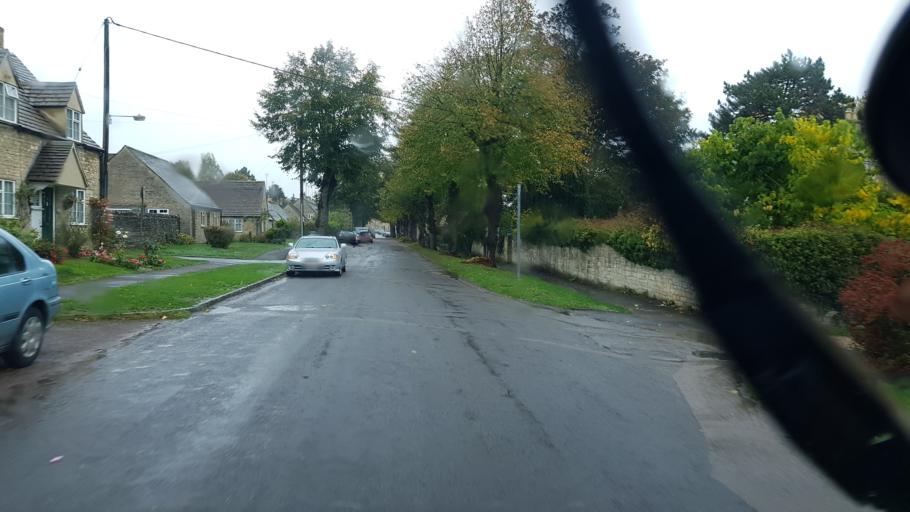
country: GB
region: England
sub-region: Oxfordshire
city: Burford
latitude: 51.8062
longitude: -1.6309
